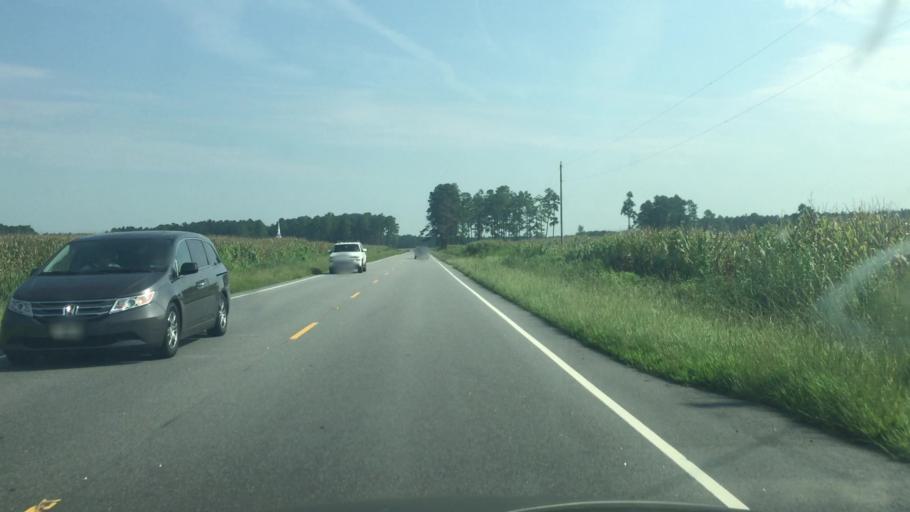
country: US
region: North Carolina
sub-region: Columbus County
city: Tabor City
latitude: 34.1711
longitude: -78.8423
